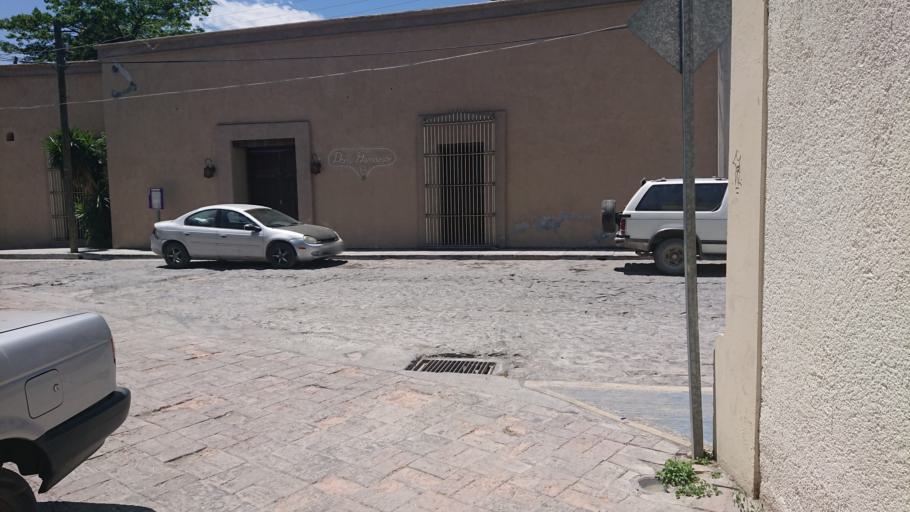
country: MX
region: Nuevo Leon
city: Garcia
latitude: 25.8110
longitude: -100.5945
